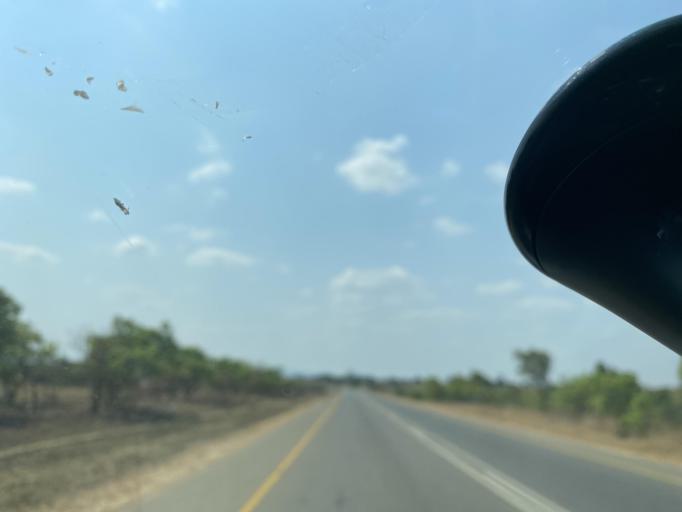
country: ZM
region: Lusaka
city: Chongwe
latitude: -15.5826
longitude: 28.7062
